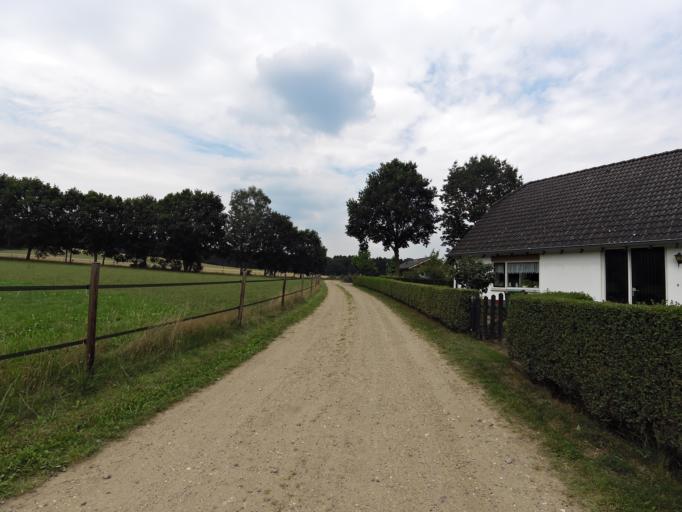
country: NL
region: Gelderland
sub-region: Gemeente Montferland
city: s-Heerenberg
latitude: 51.8827
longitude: 6.2129
